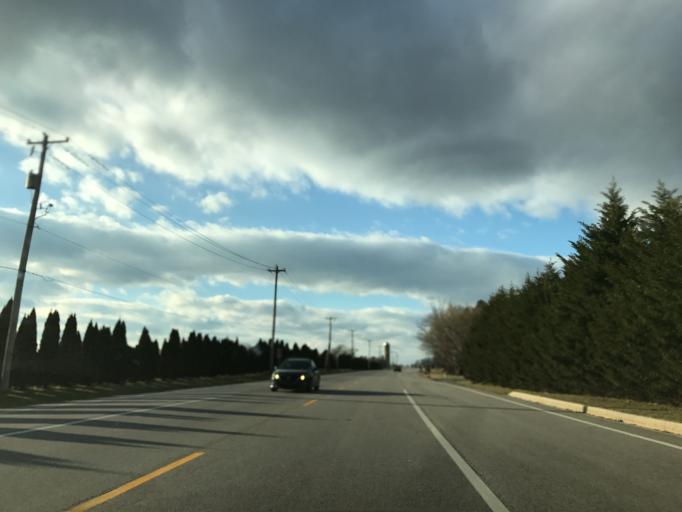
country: US
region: Maryland
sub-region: Cecil County
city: Rising Sun
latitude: 39.6581
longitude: -75.9960
